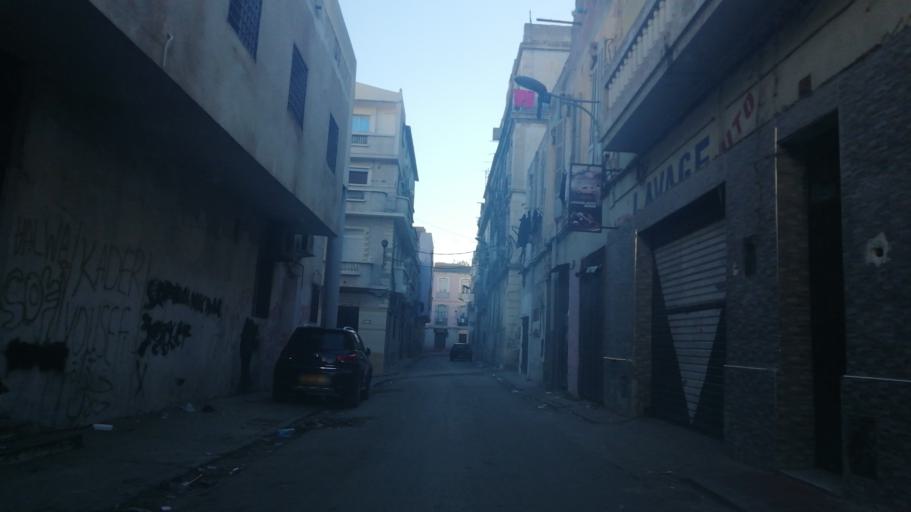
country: DZ
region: Oran
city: Oran
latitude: 35.7009
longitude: -0.6393
